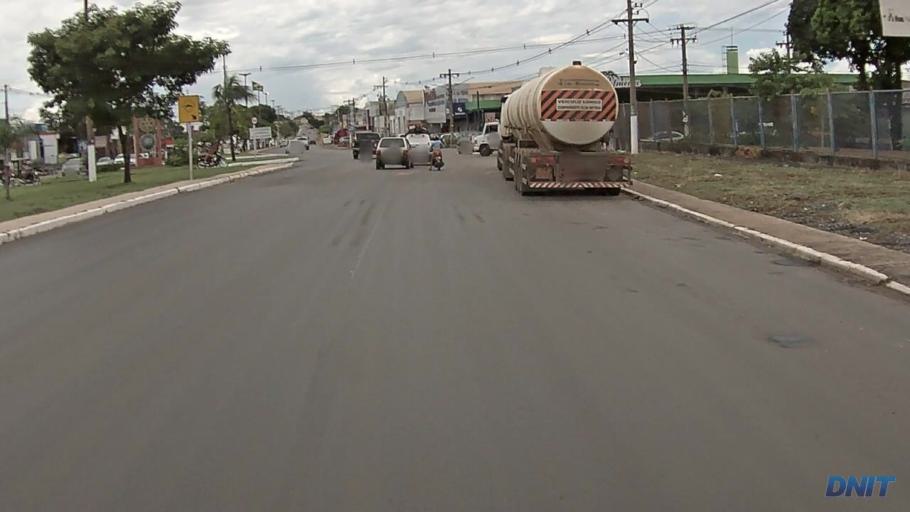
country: BR
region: Mato Grosso
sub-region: Varzea Grande
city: Varzea Grande
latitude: -15.6420
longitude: -56.1770
